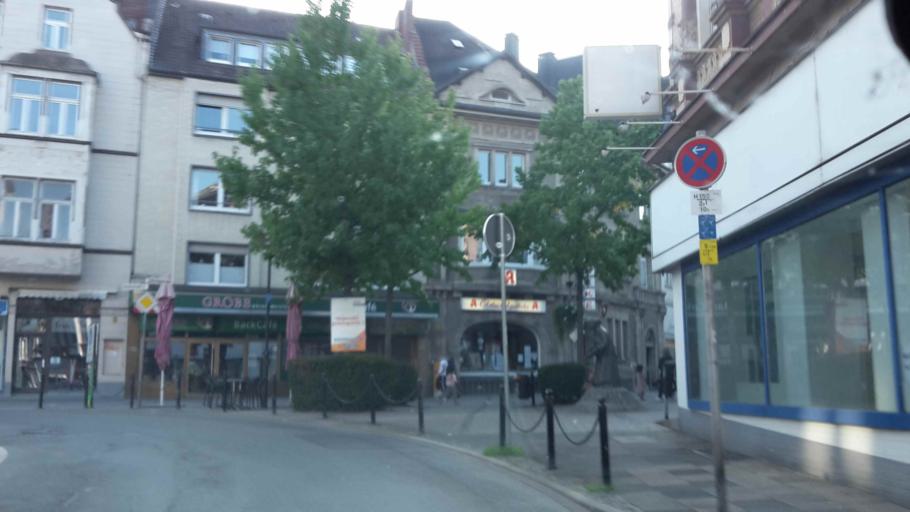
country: DE
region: North Rhine-Westphalia
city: Schwerte
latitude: 51.4412
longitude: 7.5694
